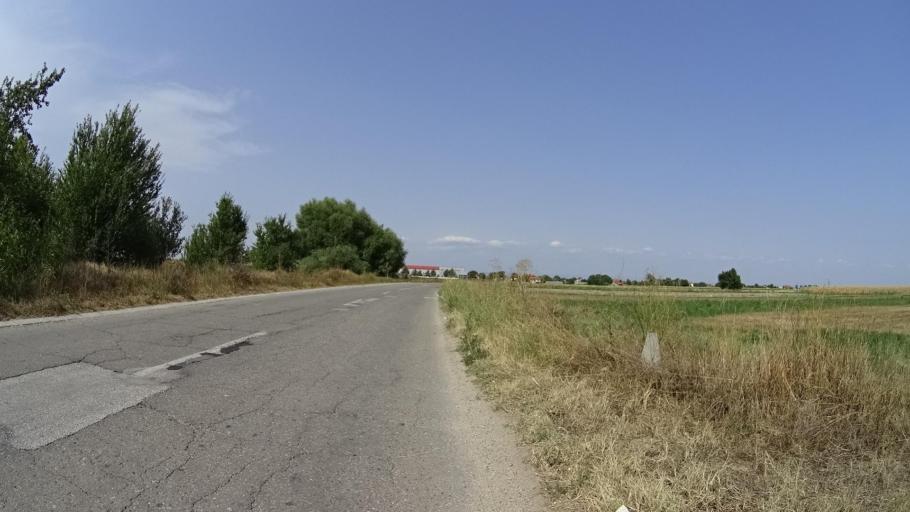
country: BG
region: Plovdiv
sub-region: Obshtina Plovdiv
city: Plovdiv
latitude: 42.2344
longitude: 24.7869
